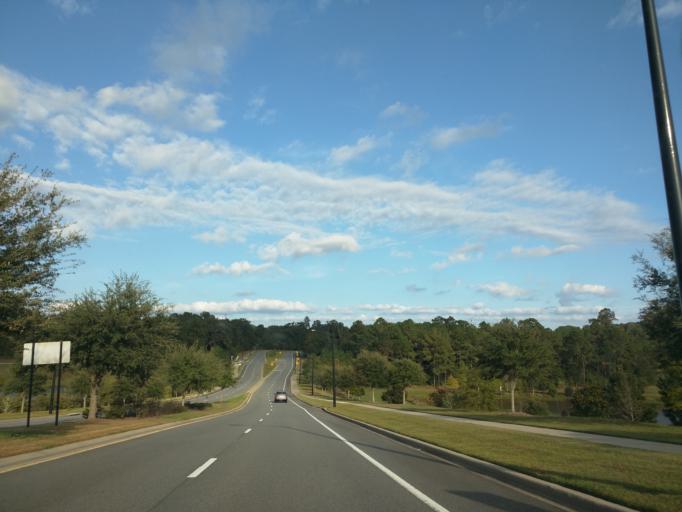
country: US
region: Florida
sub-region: Leon County
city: Tallahassee
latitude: 30.4109
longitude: -84.2337
